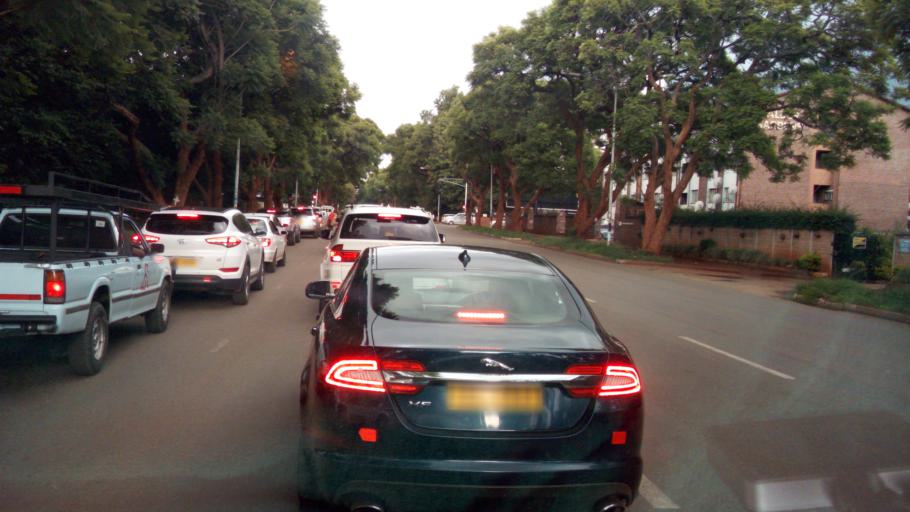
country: ZW
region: Harare
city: Harare
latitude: -17.8162
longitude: 31.0466
